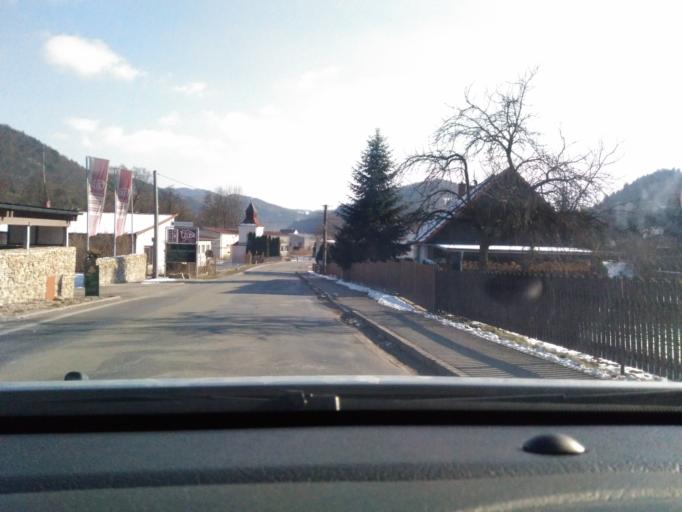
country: CZ
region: South Moravian
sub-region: Okres Brno-Venkov
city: Nedvedice
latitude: 49.4883
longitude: 16.3322
